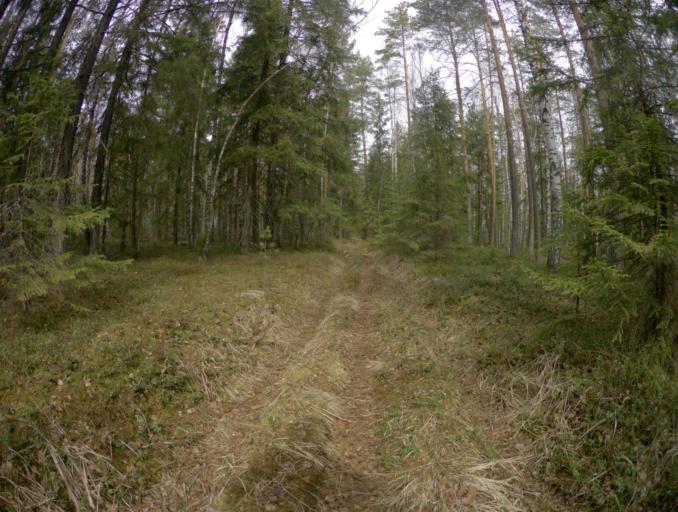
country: RU
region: Vladimir
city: Raduzhnyy
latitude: 55.9509
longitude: 40.2843
